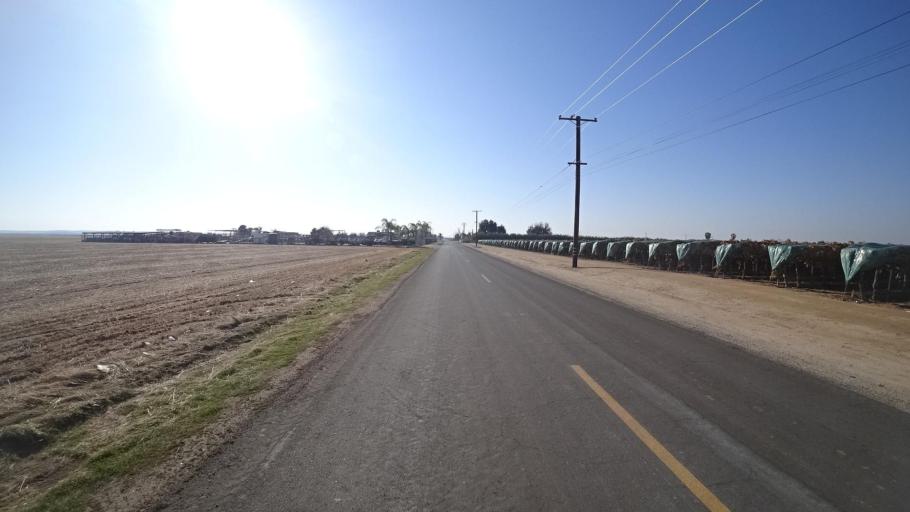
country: US
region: California
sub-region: Tulare County
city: Richgrove
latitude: 35.7523
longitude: -119.1342
